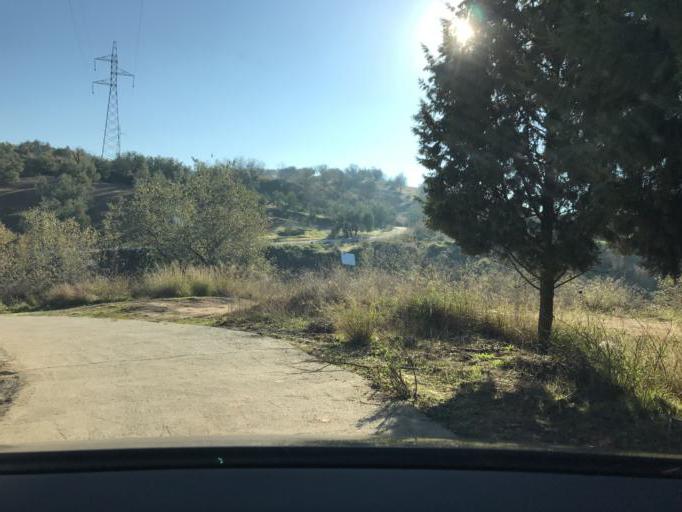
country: ES
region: Andalusia
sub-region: Provincia de Granada
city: Peligros
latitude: 37.2441
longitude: -3.6359
